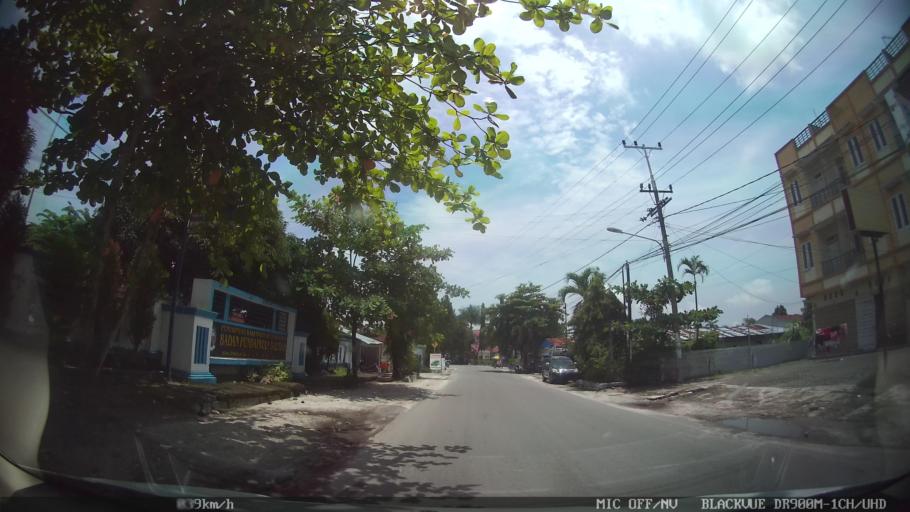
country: ID
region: North Sumatra
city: Percut
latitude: 3.5578
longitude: 98.8643
